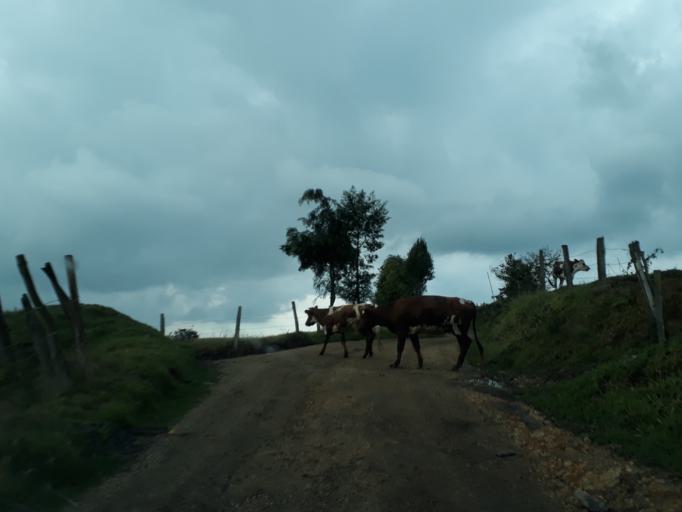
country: CO
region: Cundinamarca
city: Villapinzon
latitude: 5.2819
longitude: -73.6353
